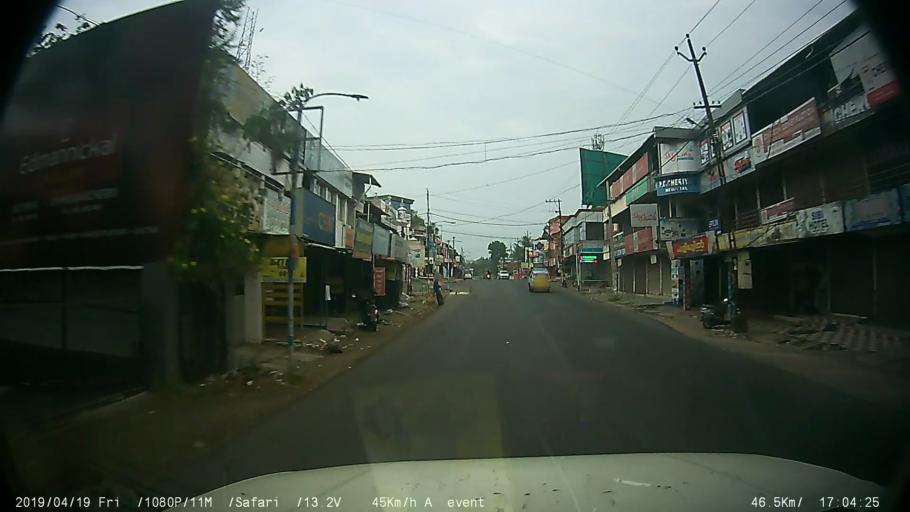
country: IN
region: Kerala
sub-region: Kottayam
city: Changanacheri
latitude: 9.4486
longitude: 76.5433
